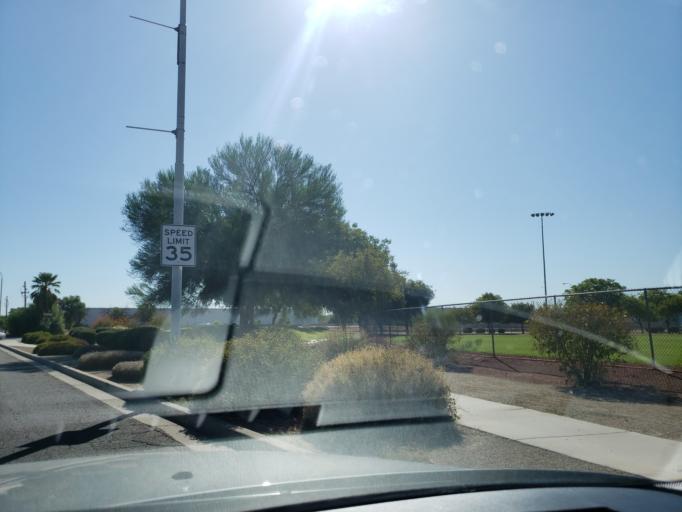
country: US
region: Arizona
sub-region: Maricopa County
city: Tolleson
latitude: 33.4512
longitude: -112.2451
